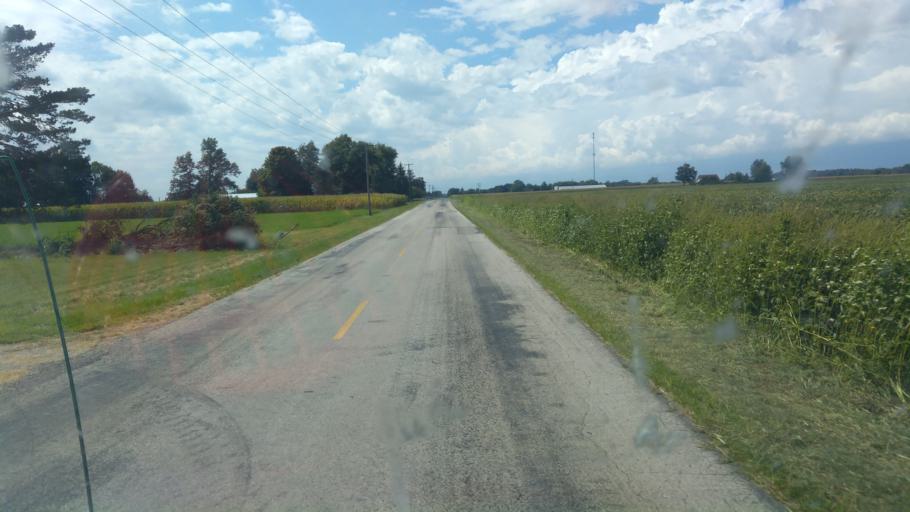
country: US
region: Ohio
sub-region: Union County
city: Richwood
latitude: 40.6002
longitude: -83.3734
